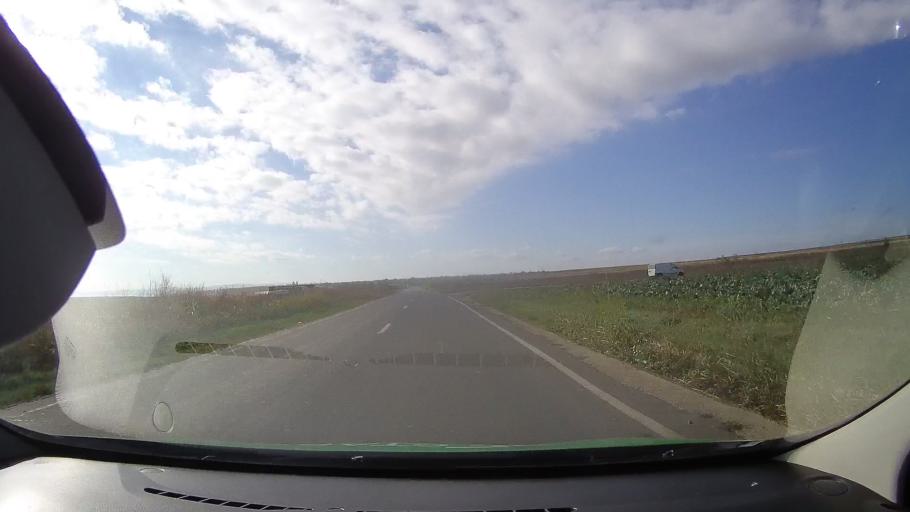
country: RO
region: Tulcea
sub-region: Comuna Sarichioi
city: Sarichioi
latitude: 44.9658
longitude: 28.8649
